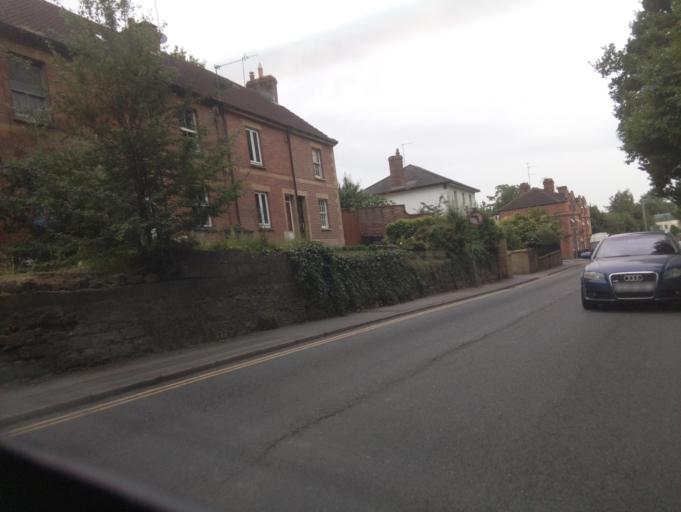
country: GB
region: England
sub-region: Somerset
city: Yeovil
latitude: 50.9473
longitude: -2.6366
